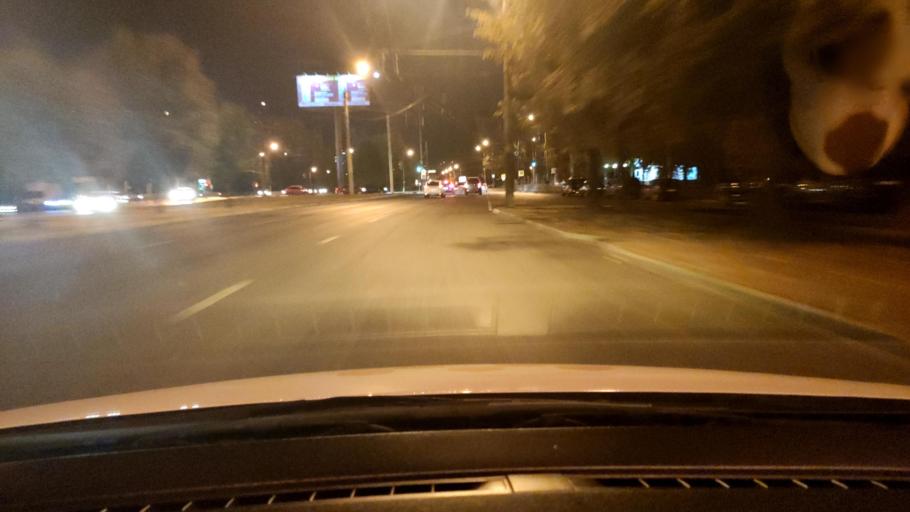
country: RU
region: Voronezj
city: Podgornoye
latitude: 51.7124
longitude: 39.1710
